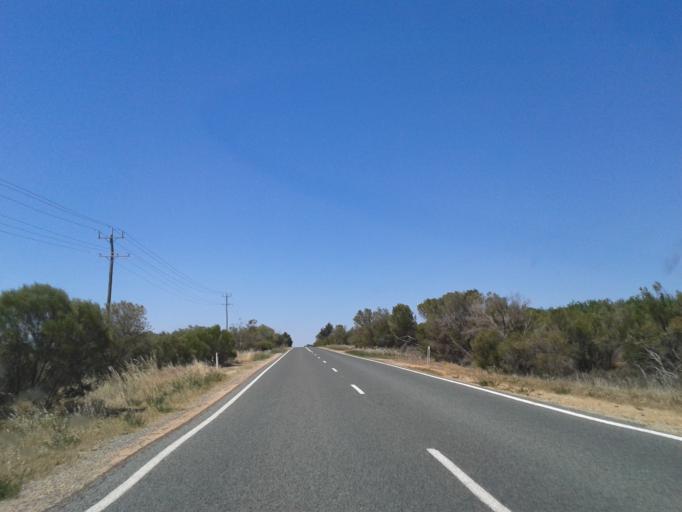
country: AU
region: Victoria
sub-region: Mildura Shire
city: Ouyen
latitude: -34.7121
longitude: 142.9325
